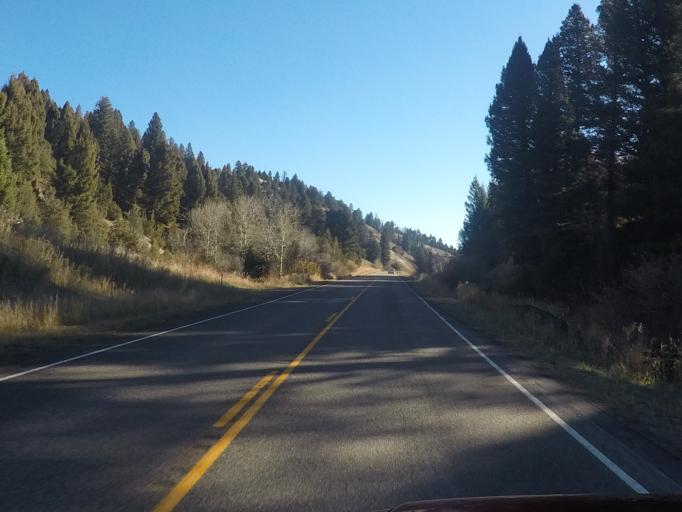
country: US
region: Montana
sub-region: Meagher County
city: White Sulphur Springs
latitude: 46.3580
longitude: -111.1125
